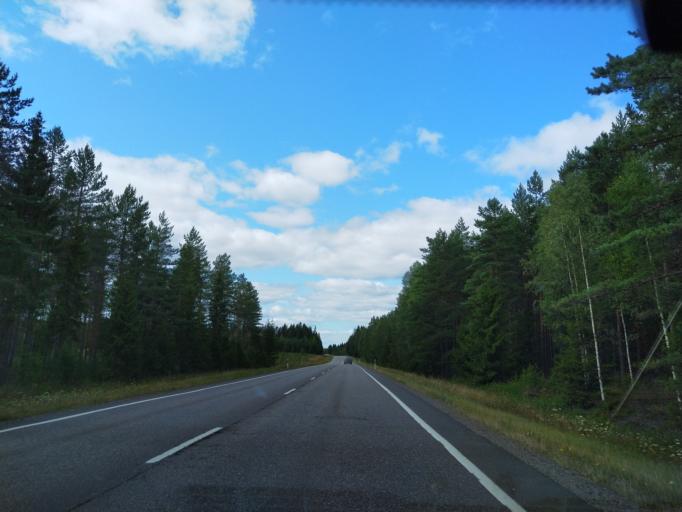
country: FI
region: Haeme
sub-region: Haemeenlinna
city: Renko
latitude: 60.7637
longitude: 24.2694
